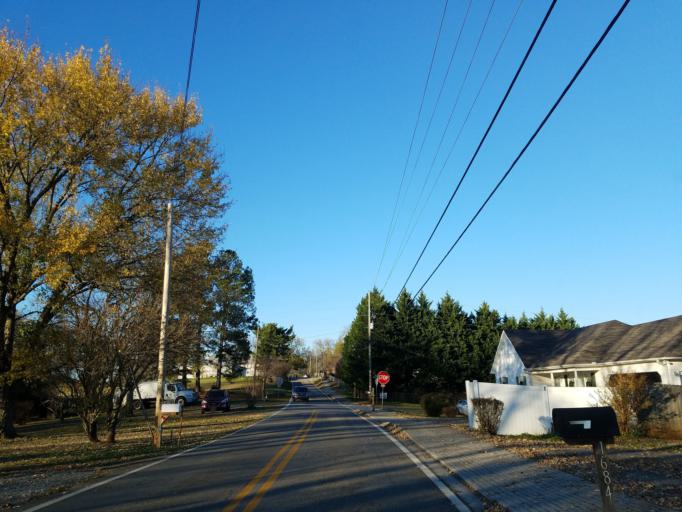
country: US
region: Georgia
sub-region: Pickens County
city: Nelson
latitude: 34.3777
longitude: -84.3657
